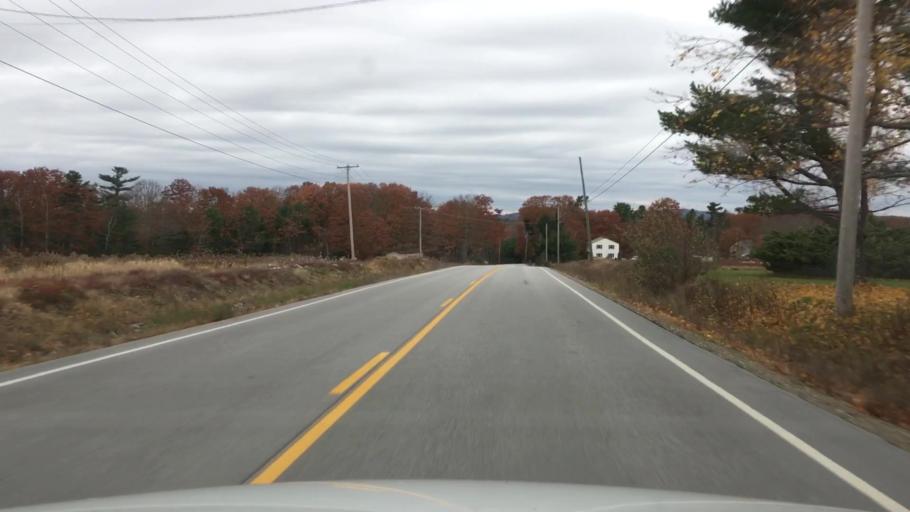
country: US
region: Maine
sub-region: Hancock County
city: Orland
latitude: 44.5527
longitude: -68.6934
